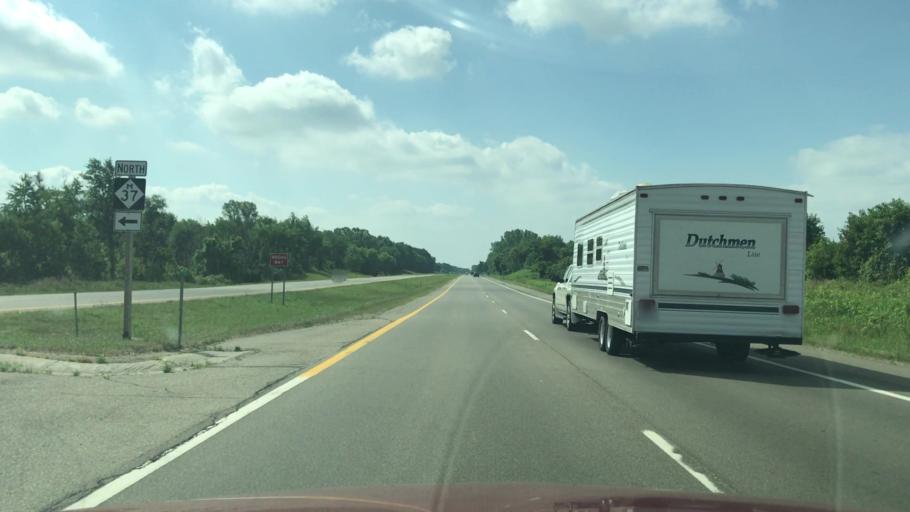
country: US
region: Michigan
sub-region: Kent County
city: Sparta
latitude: 43.1154
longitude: -85.7048
